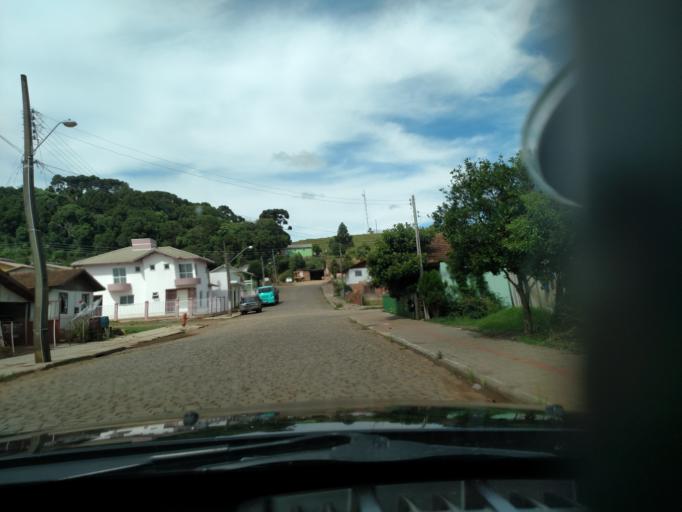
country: BR
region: Rio Grande do Sul
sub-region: Vacaria
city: Estrela
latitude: -27.8971
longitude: -50.7568
